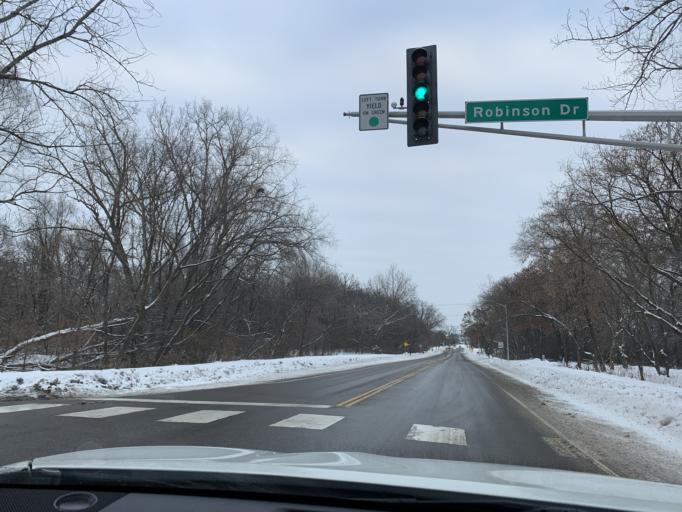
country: US
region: Minnesota
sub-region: Anoka County
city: Coon Rapids
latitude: 45.1607
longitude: -93.2987
